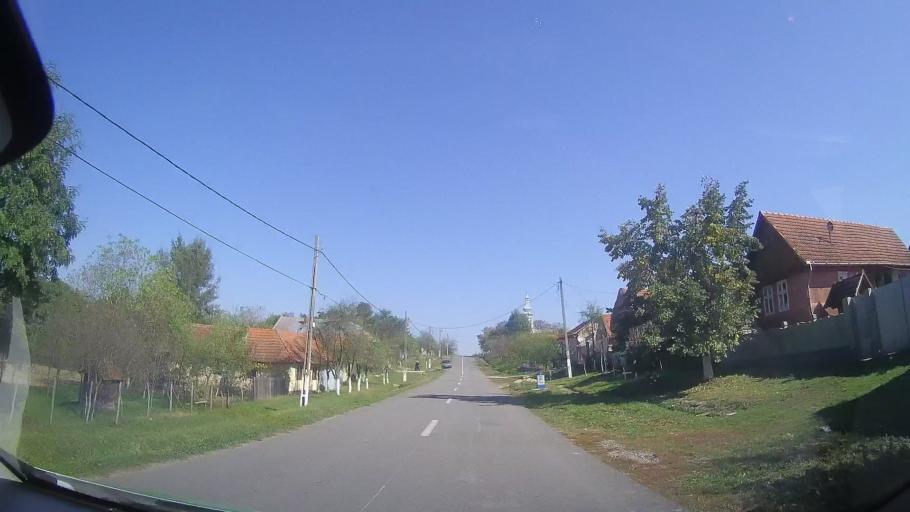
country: RO
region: Timis
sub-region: Comuna Balint
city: Balint
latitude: 45.8452
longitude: 21.8628
